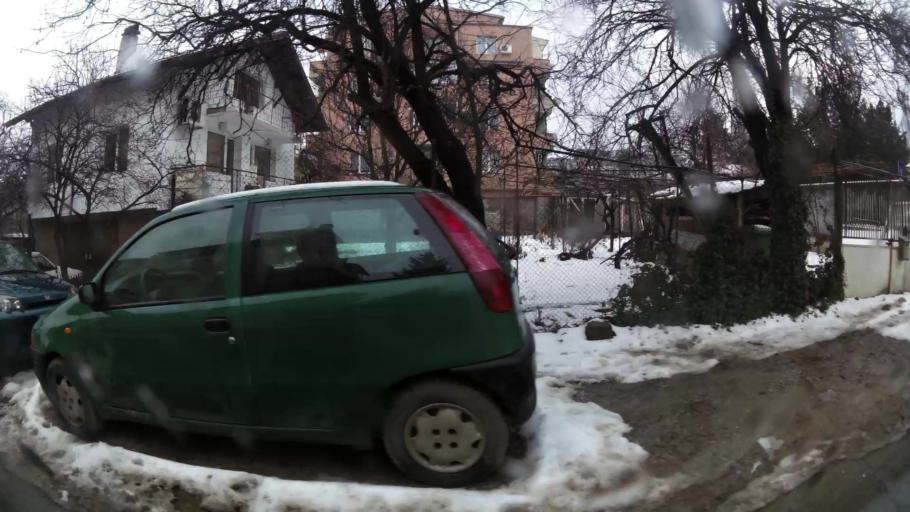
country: BG
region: Sofia-Capital
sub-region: Stolichna Obshtina
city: Sofia
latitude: 42.6576
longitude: 23.2774
